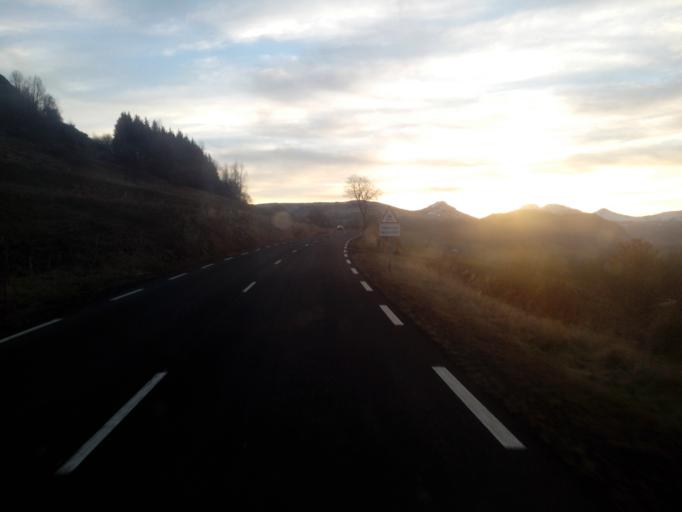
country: FR
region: Auvergne
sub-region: Departement du Cantal
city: Murat
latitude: 45.1669
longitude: 2.8346
